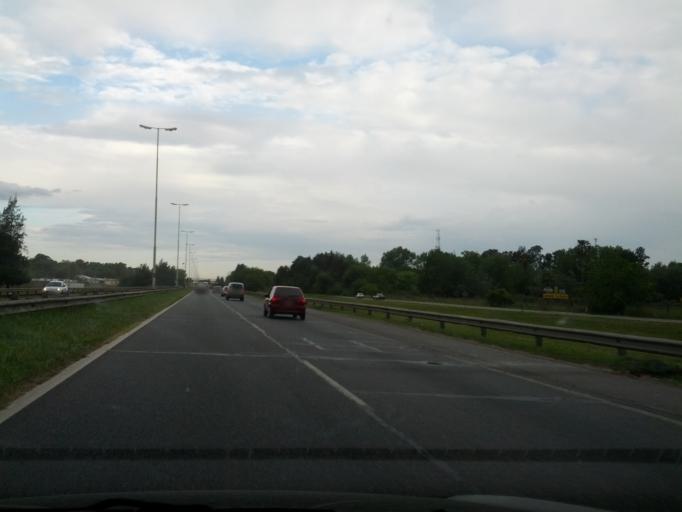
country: AR
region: Buenos Aires
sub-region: Partido de General Rodriguez
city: General Rodriguez
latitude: -34.5891
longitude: -58.9663
